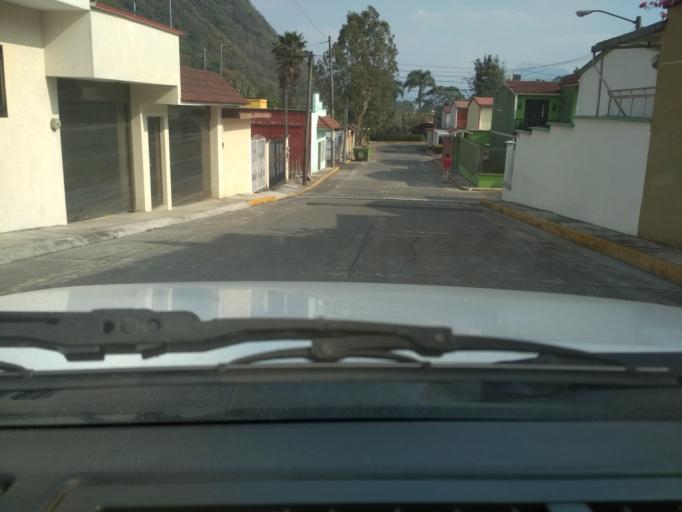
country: MX
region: Veracruz
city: Orizaba
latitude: 18.8666
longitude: -97.0947
